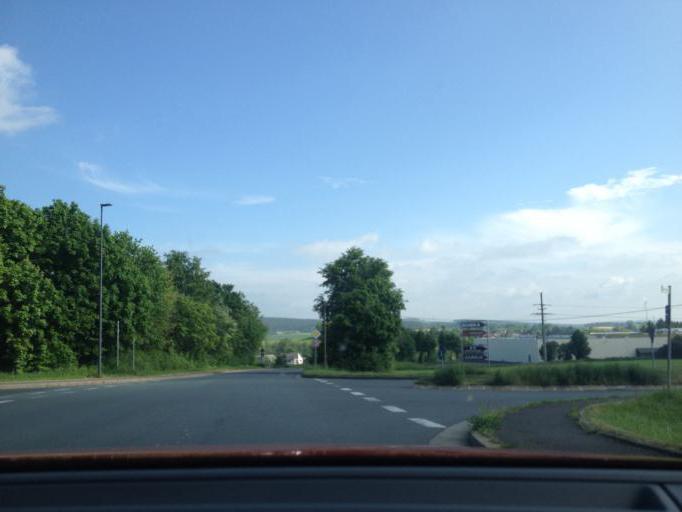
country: DE
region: Bavaria
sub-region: Upper Franconia
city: Marktredwitz
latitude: 50.0151
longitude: 12.0959
